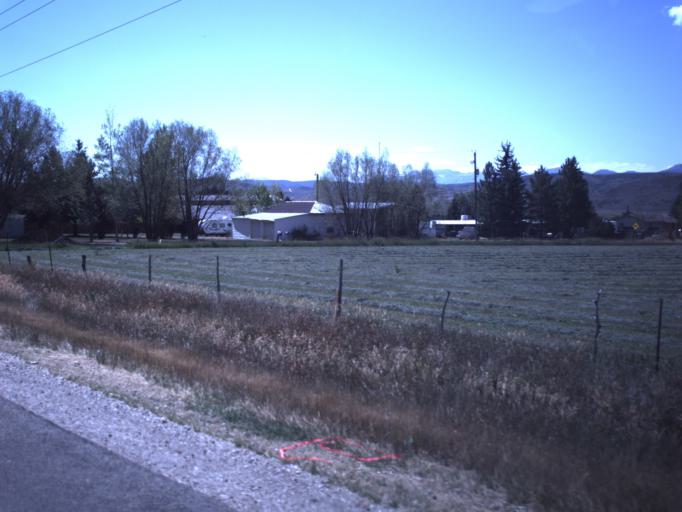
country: US
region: Utah
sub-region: Summit County
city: Kamas
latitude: 40.6813
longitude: -111.2810
